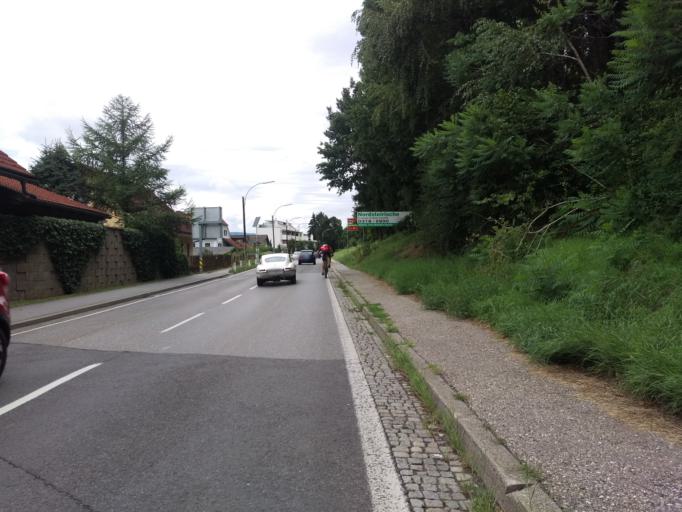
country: AT
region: Styria
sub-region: Politischer Bezirk Graz-Umgebung
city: Raaba
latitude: 47.0362
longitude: 15.4922
